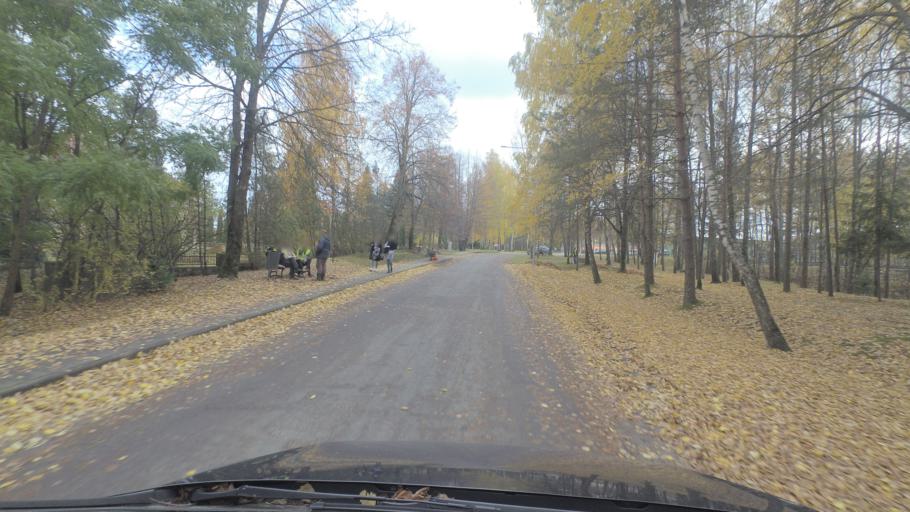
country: LT
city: Ignalina
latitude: 55.3399
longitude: 26.1400
